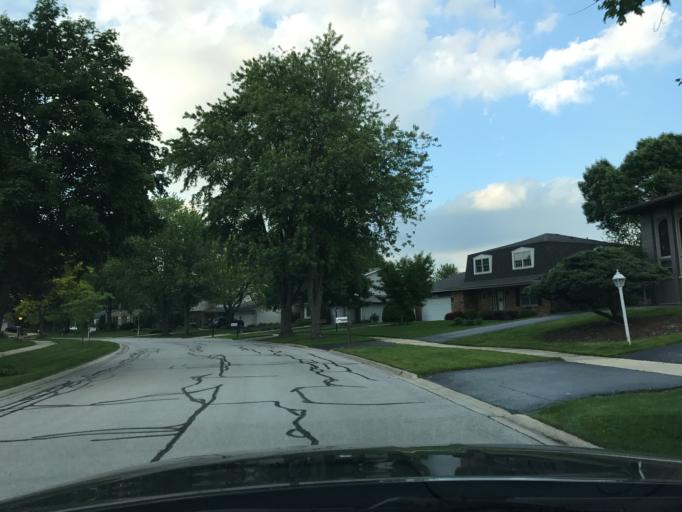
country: US
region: Illinois
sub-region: DuPage County
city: Naperville
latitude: 41.7748
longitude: -88.1113
